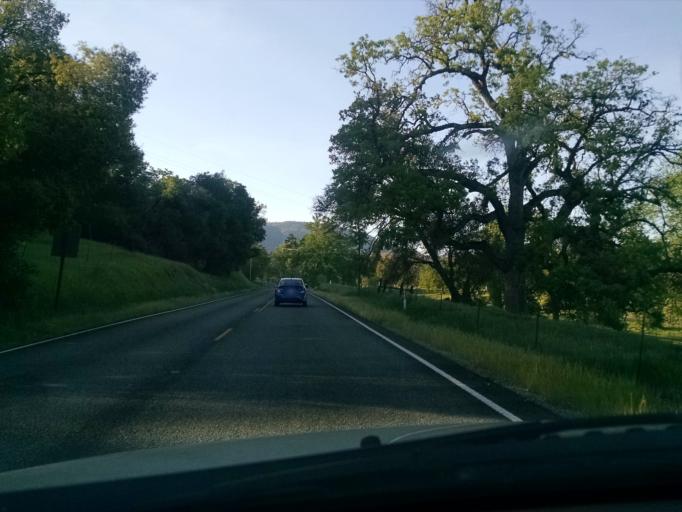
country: US
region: California
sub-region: Madera County
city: Ahwahnee
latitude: 37.3779
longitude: -119.7308
